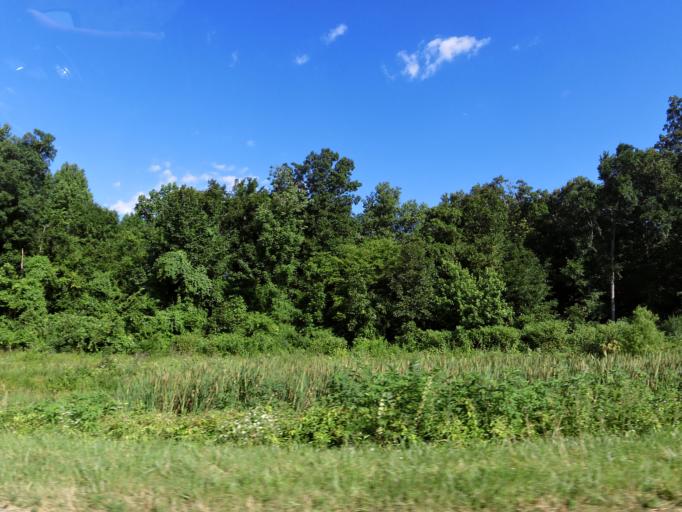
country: US
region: Arkansas
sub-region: Clay County
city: Corning
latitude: 36.5350
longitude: -90.5323
